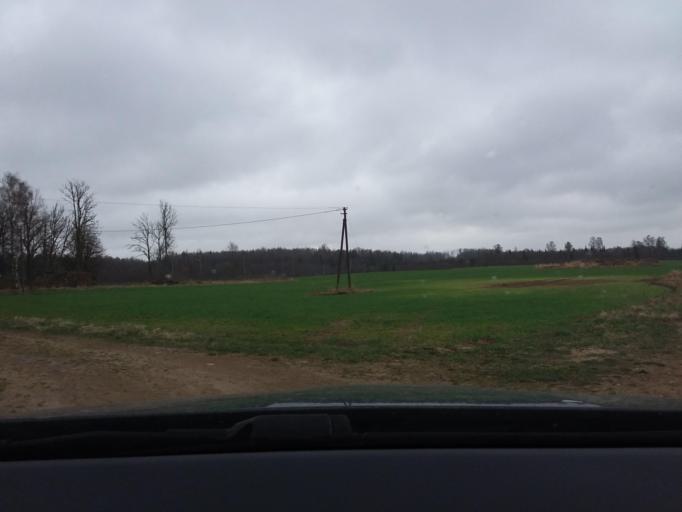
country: LV
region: Broceni
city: Broceni
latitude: 56.7402
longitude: 22.4850
